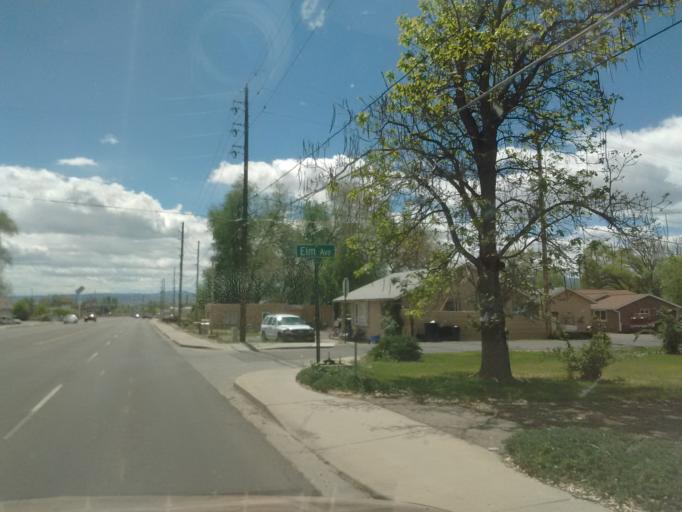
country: US
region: Colorado
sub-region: Mesa County
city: Fruitvale
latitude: 39.0810
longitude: -108.4966
